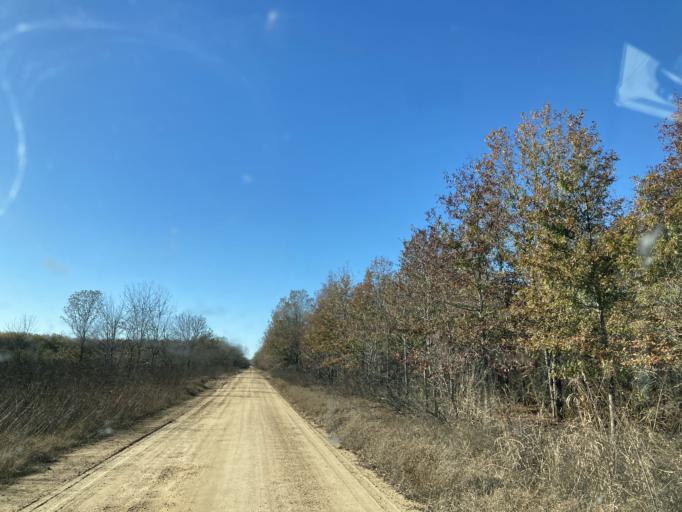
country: US
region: Mississippi
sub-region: Sharkey County
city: Rolling Fork
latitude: 32.7491
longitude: -90.6731
